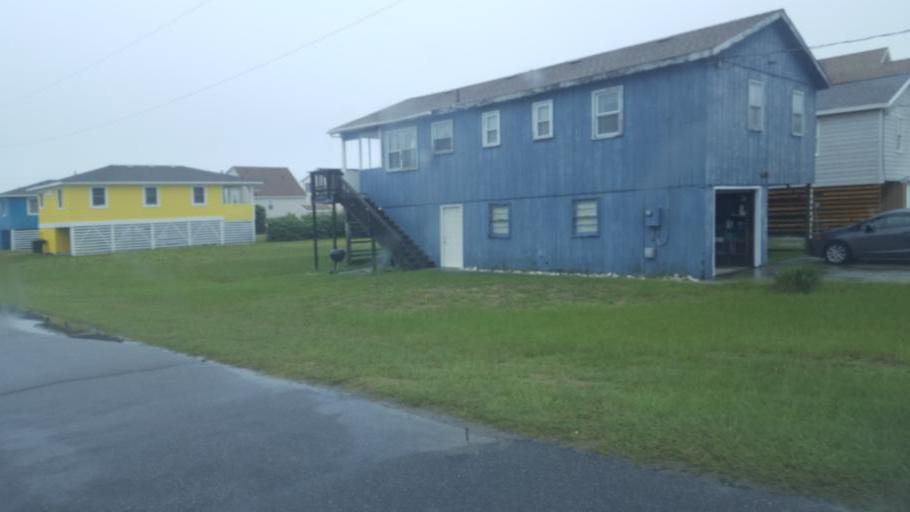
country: US
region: North Carolina
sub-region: Dare County
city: Kitty Hawk
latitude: 36.0785
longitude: -75.6996
